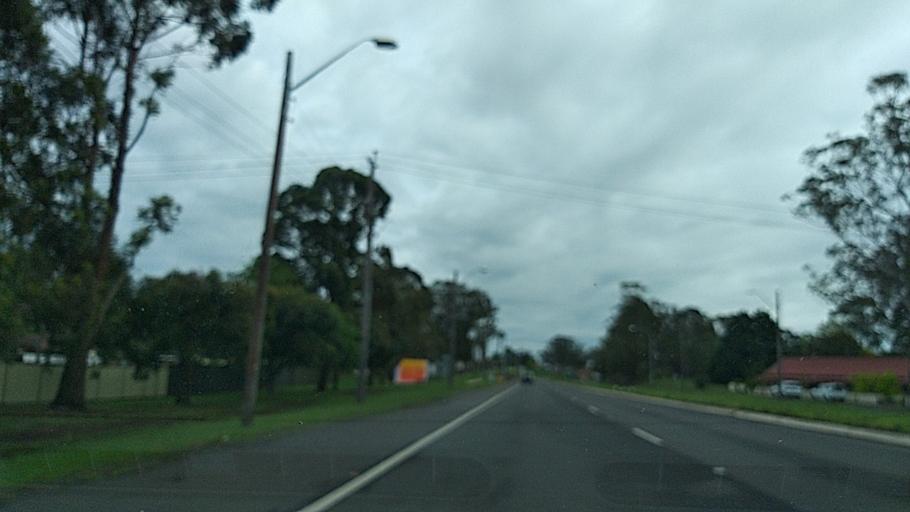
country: AU
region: New South Wales
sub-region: Camden
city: Camden South
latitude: -34.0792
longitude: 150.6947
